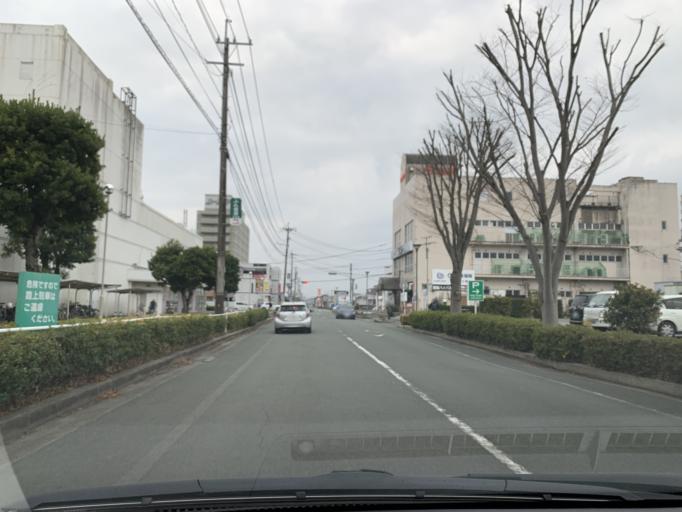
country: JP
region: Kumamoto
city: Ozu
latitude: 32.8765
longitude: 130.8667
